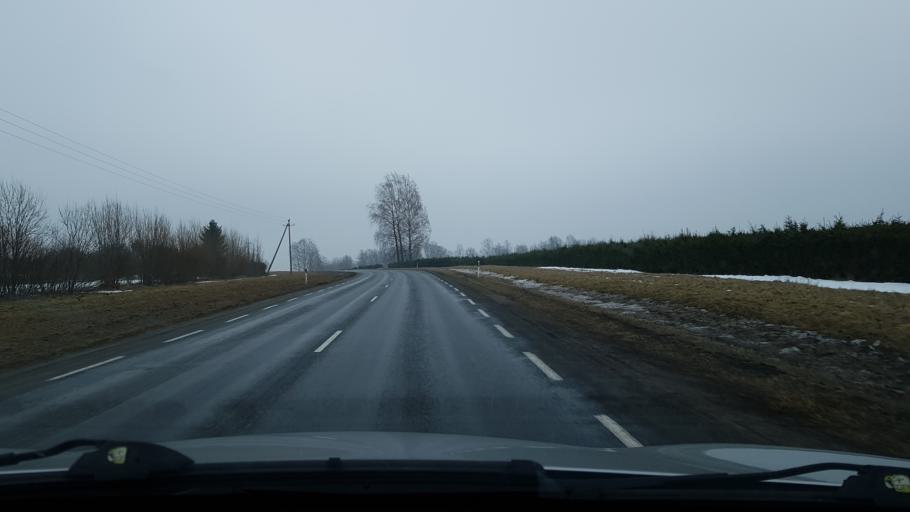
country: EE
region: Viljandimaa
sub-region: Viiratsi vald
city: Viiratsi
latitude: 58.2509
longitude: 25.8273
